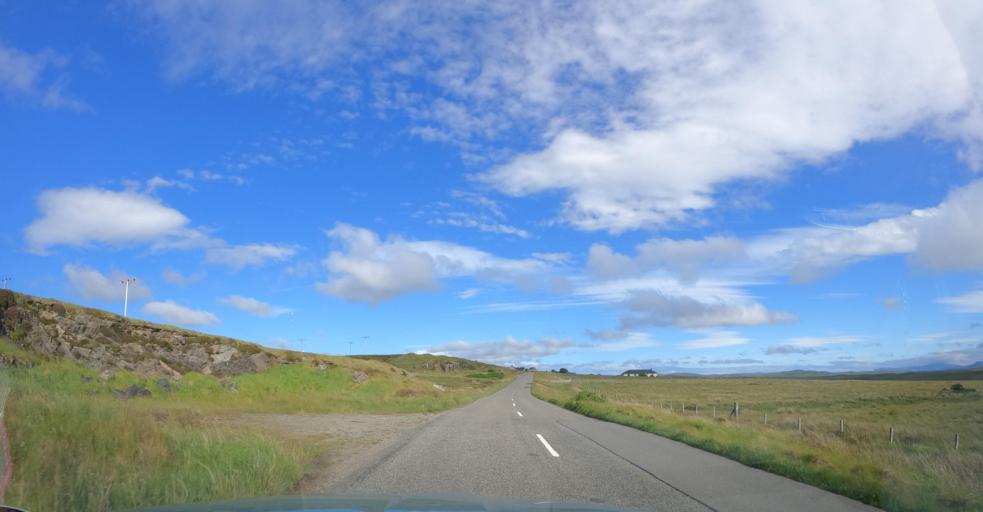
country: GB
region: Scotland
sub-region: Eilean Siar
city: Stornoway
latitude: 58.1764
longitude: -6.6176
